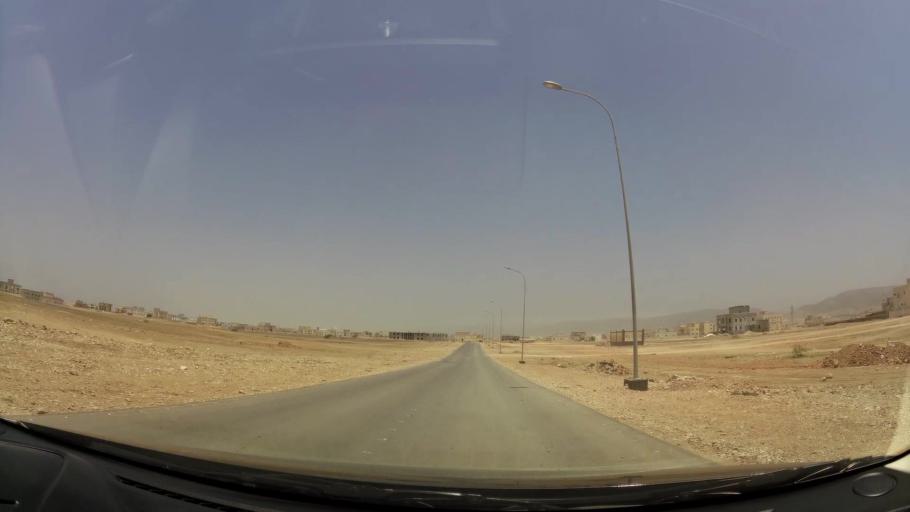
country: OM
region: Zufar
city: Salalah
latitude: 17.0976
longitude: 54.1764
